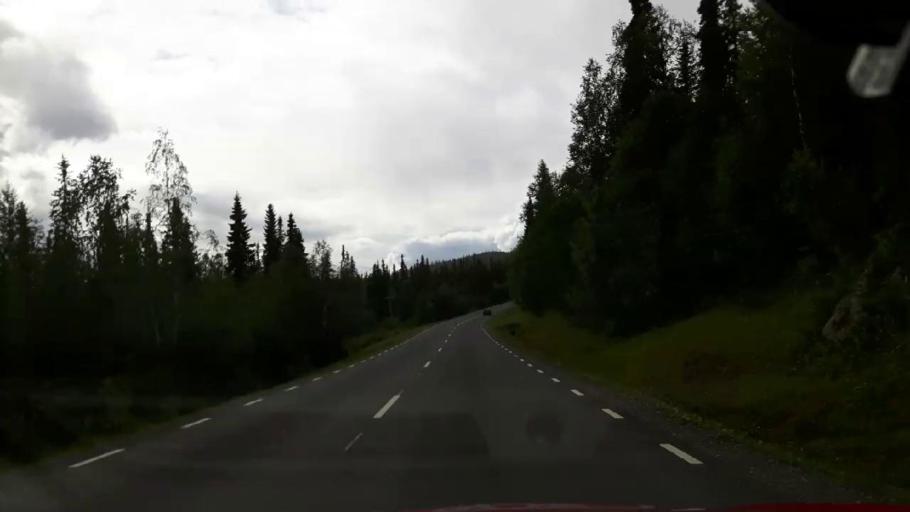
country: NO
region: Nord-Trondelag
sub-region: Royrvik
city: Royrvik
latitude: 64.8664
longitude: 14.1931
